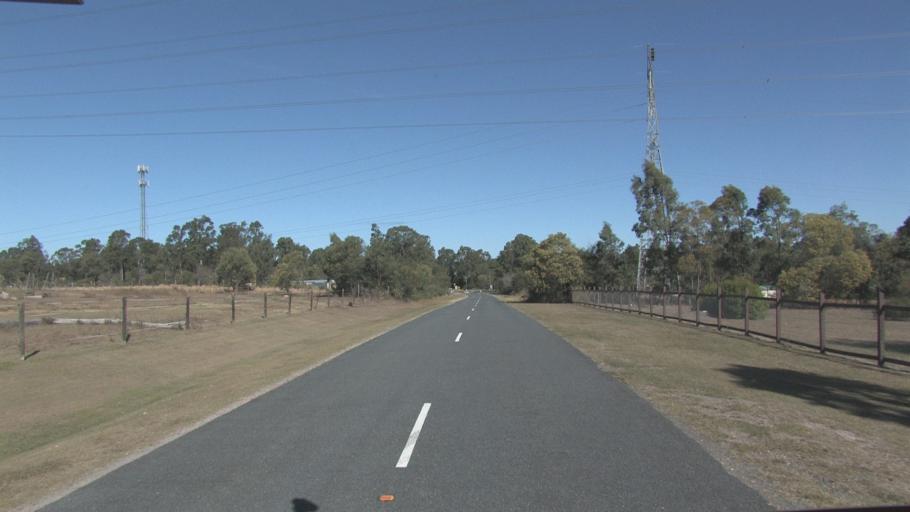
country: AU
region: Queensland
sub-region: Logan
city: North Maclean
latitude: -27.7327
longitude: 152.9608
